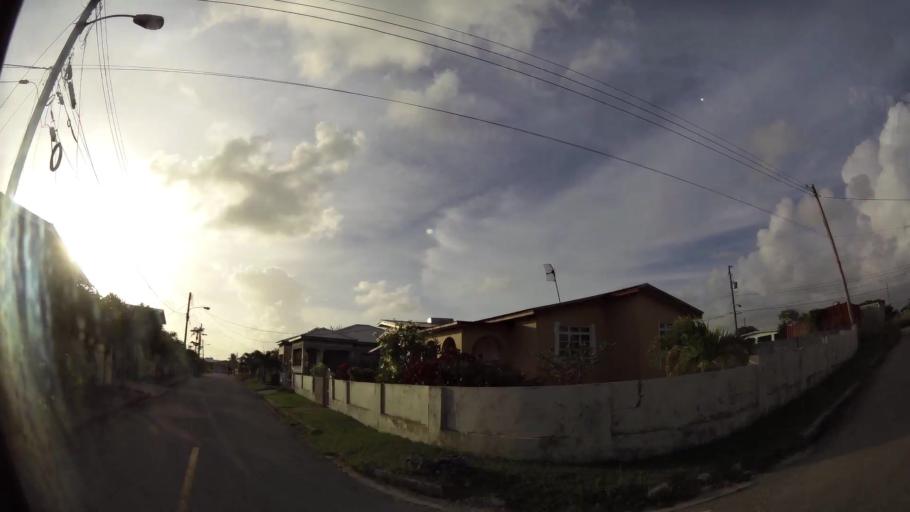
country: BB
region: Christ Church
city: Oistins
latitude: 13.0550
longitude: -59.5116
